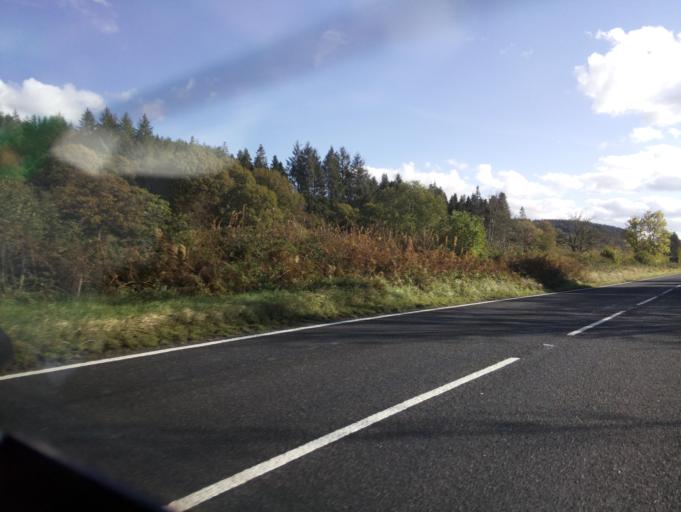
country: GB
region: Wales
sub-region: Merthyr Tydfil County Borough
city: Merthyr Tydfil
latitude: 51.8115
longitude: -3.4441
